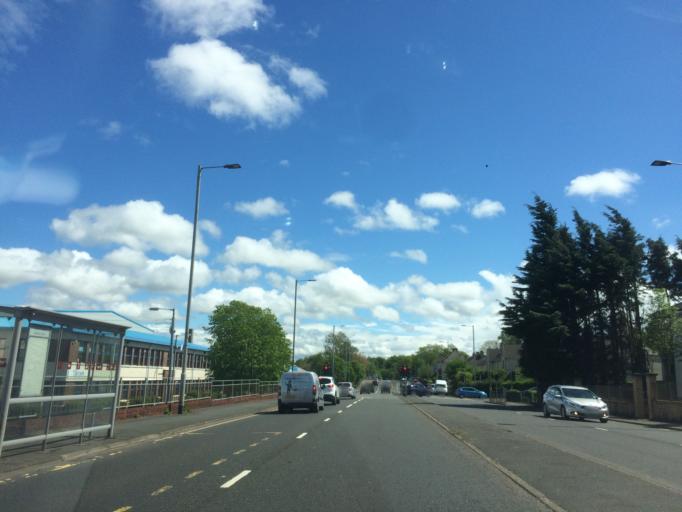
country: GB
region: Scotland
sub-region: East Renfrewshire
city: Newton Mearns
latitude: 55.8019
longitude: -4.3294
